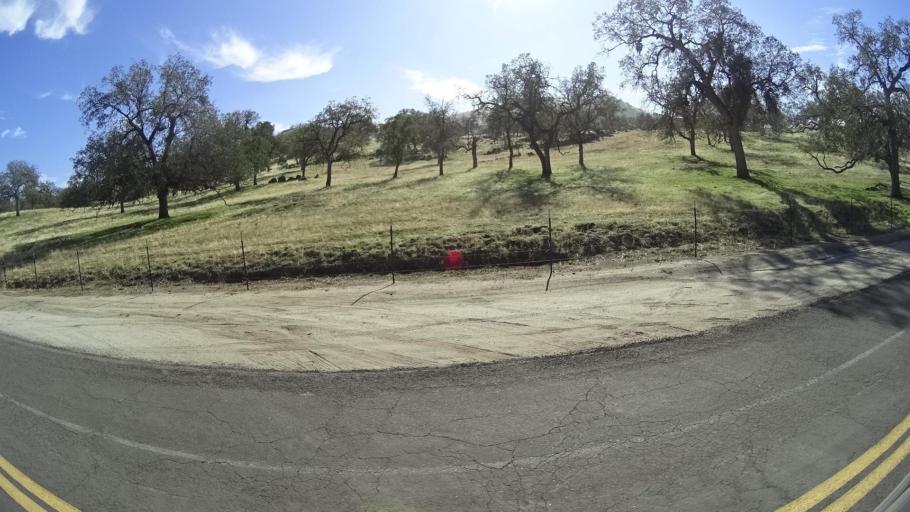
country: US
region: California
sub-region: Tulare County
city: Richgrove
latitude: 35.6998
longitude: -118.8463
